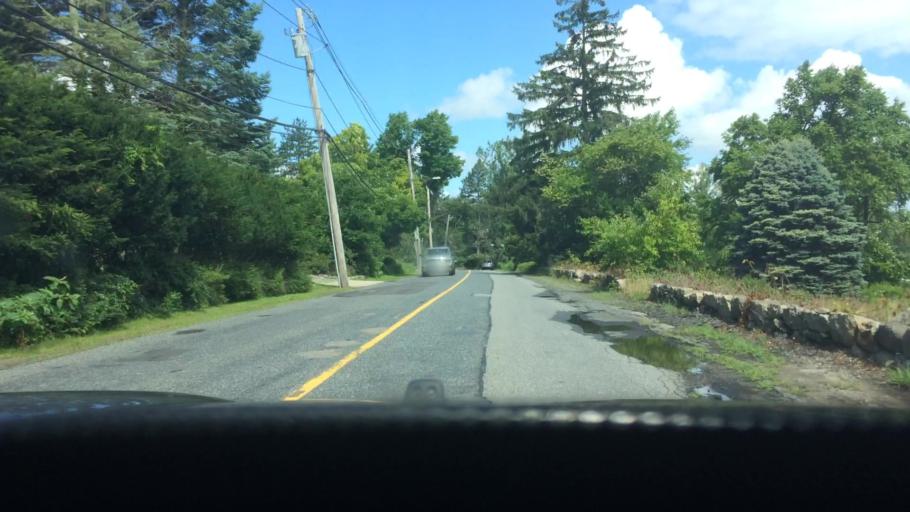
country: US
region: Massachusetts
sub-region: Middlesex County
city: Weston
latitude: 42.3567
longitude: -71.2930
